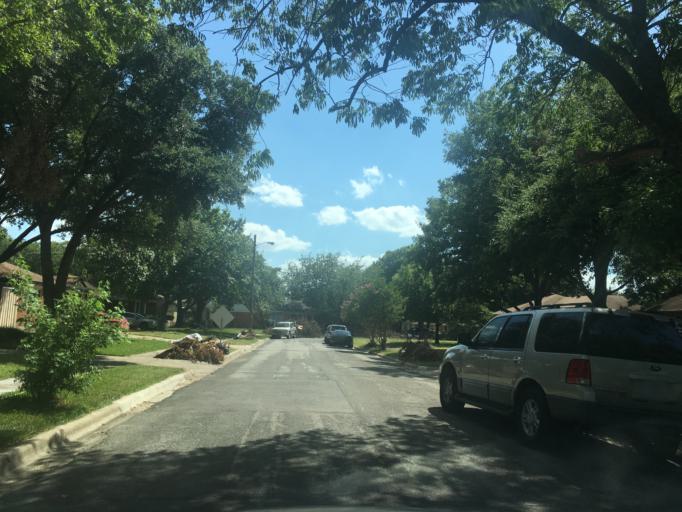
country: US
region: Texas
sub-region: Dallas County
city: Garland
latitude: 32.8357
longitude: -96.6795
